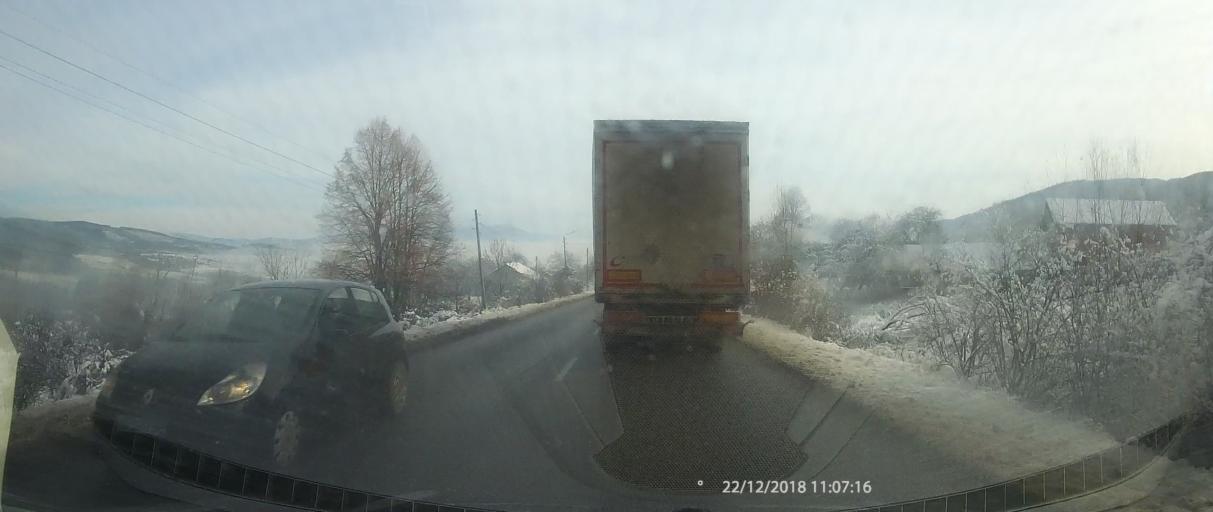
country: BG
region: Kyustendil
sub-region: Obshtina Kyustendil
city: Kyustendil
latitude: 42.2640
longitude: 22.5925
